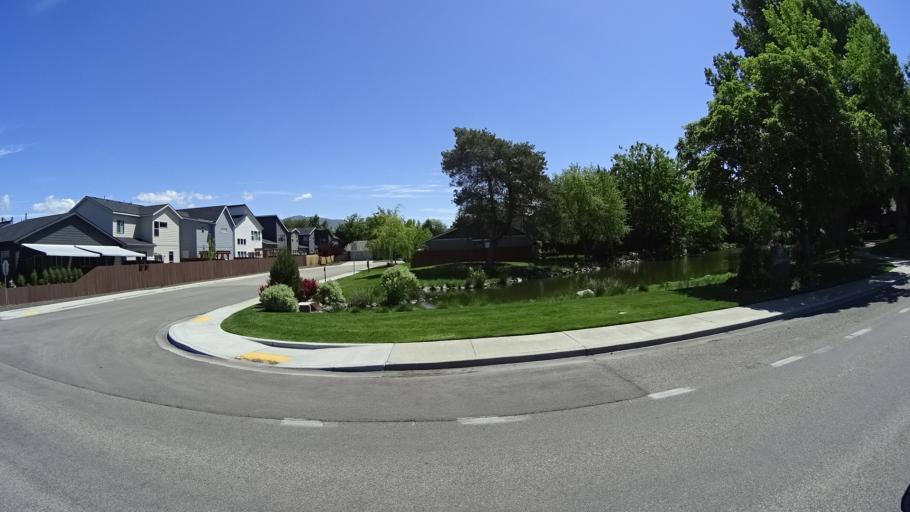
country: US
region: Idaho
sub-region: Ada County
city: Boise
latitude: 43.5778
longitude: -116.1836
